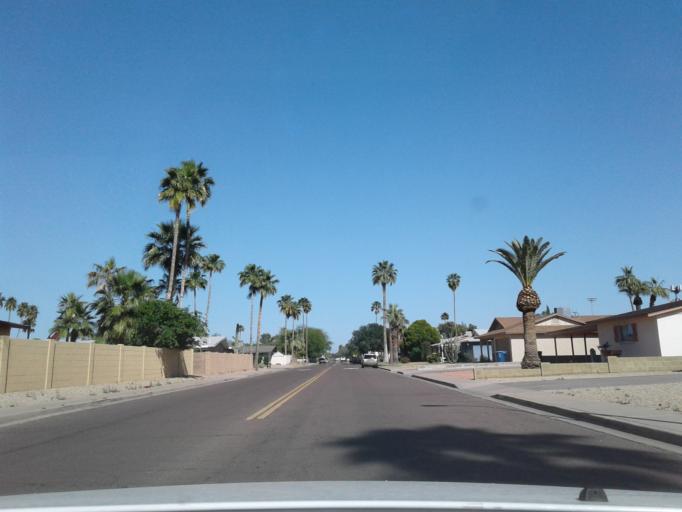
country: US
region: Arizona
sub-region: Maricopa County
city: Tempe
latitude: 33.4001
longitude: -111.9075
